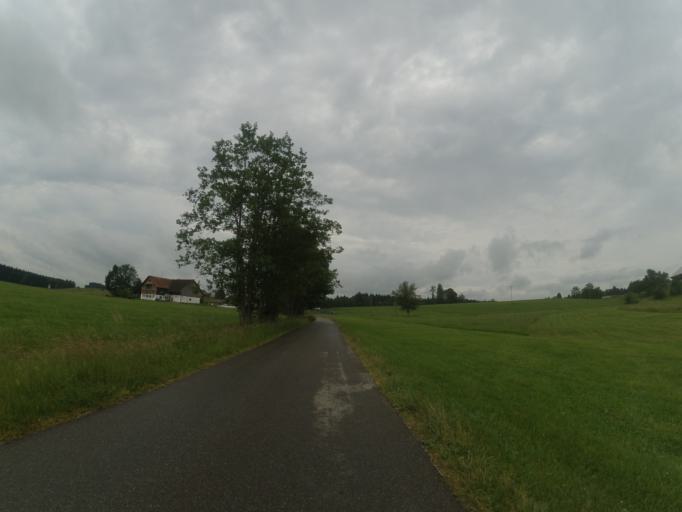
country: DE
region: Baden-Wuerttemberg
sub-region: Tuebingen Region
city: Kisslegg
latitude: 47.7577
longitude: 9.8507
